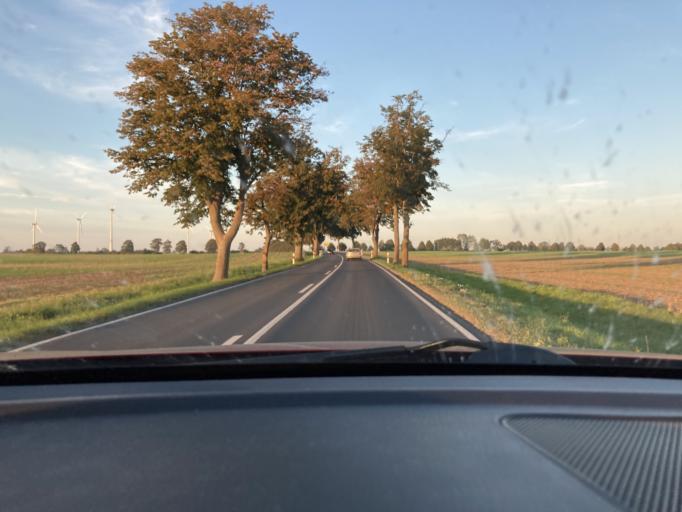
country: DE
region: Mecklenburg-Vorpommern
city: Alt-Sanitz
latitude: 53.7621
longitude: 13.6404
